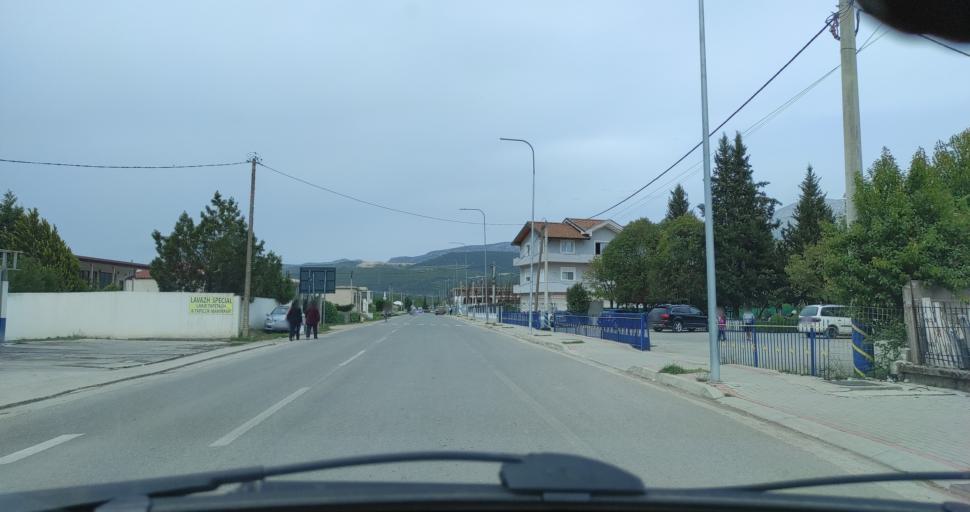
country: AL
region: Durres
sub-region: Rrethi i Krujes
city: Fushe-Kruje
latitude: 41.4833
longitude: 19.7237
